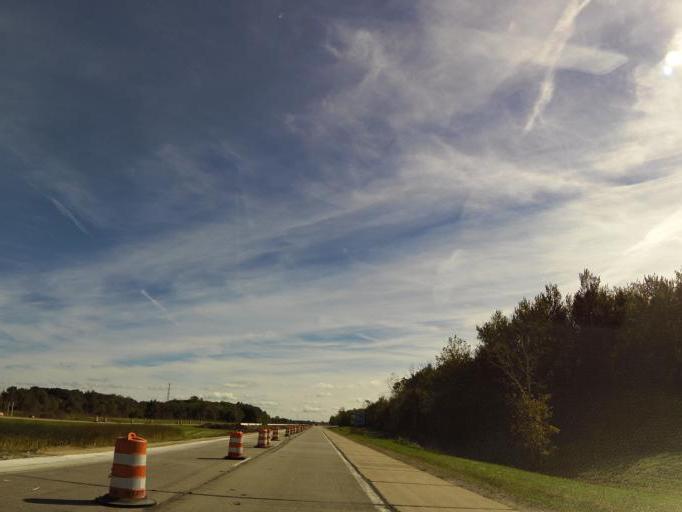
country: US
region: Michigan
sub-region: Macomb County
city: Memphis
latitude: 42.9786
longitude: -82.7815
